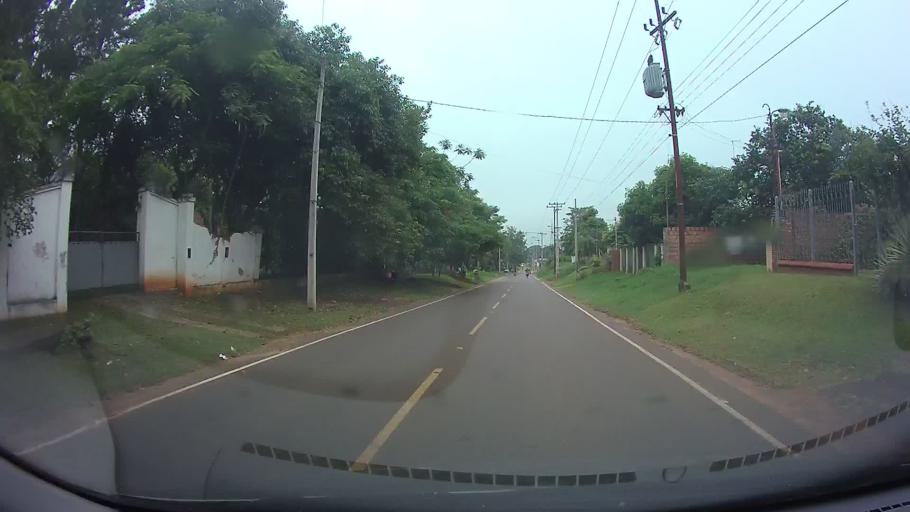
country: PY
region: Central
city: Itaugua
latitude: -25.3780
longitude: -57.3492
